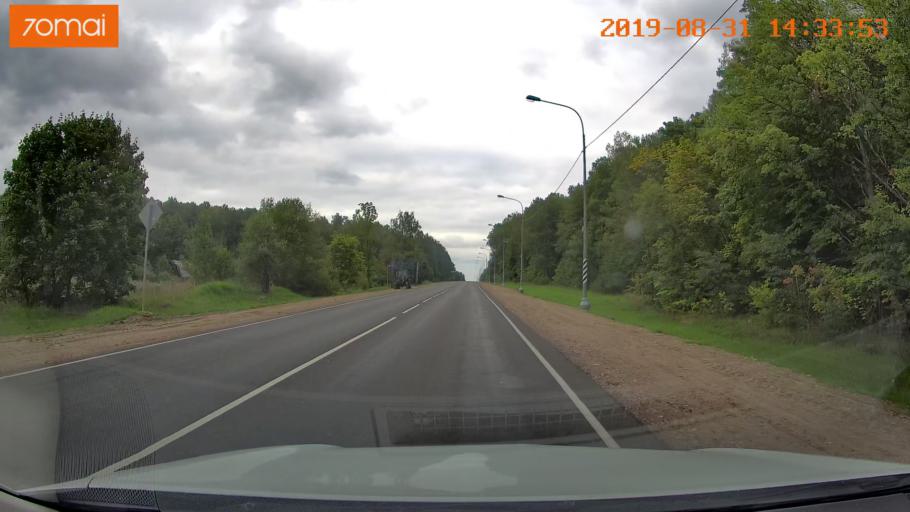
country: RU
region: Smolensk
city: Yekimovichi
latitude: 54.1545
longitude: 33.4276
